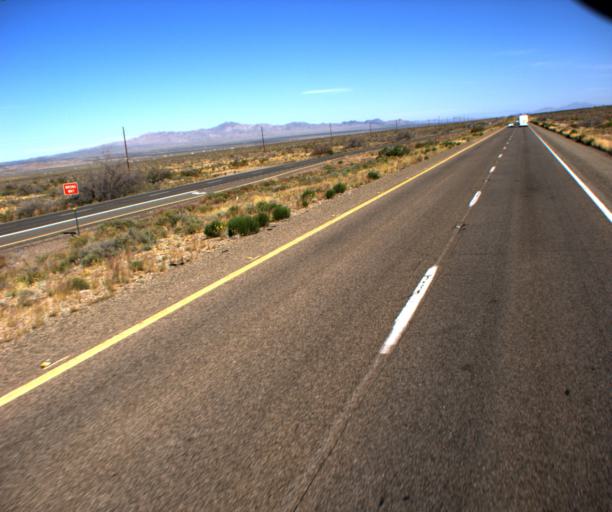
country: US
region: Arizona
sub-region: Mohave County
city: Dolan Springs
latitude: 35.4565
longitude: -114.3017
